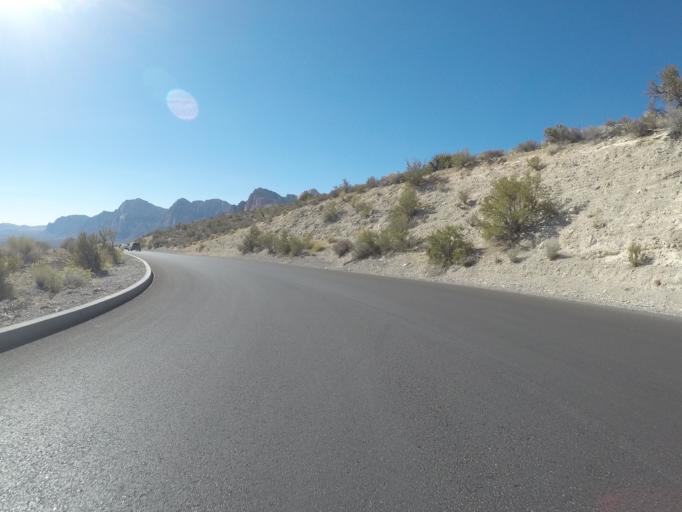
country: US
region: Nevada
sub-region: Clark County
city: Summerlin South
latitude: 36.1715
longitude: -115.4705
